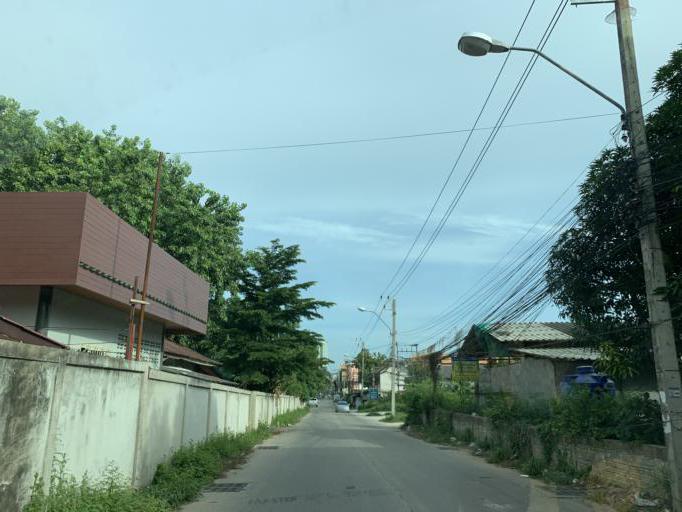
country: TH
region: Chon Buri
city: Phatthaya
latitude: 12.9051
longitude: 100.8743
